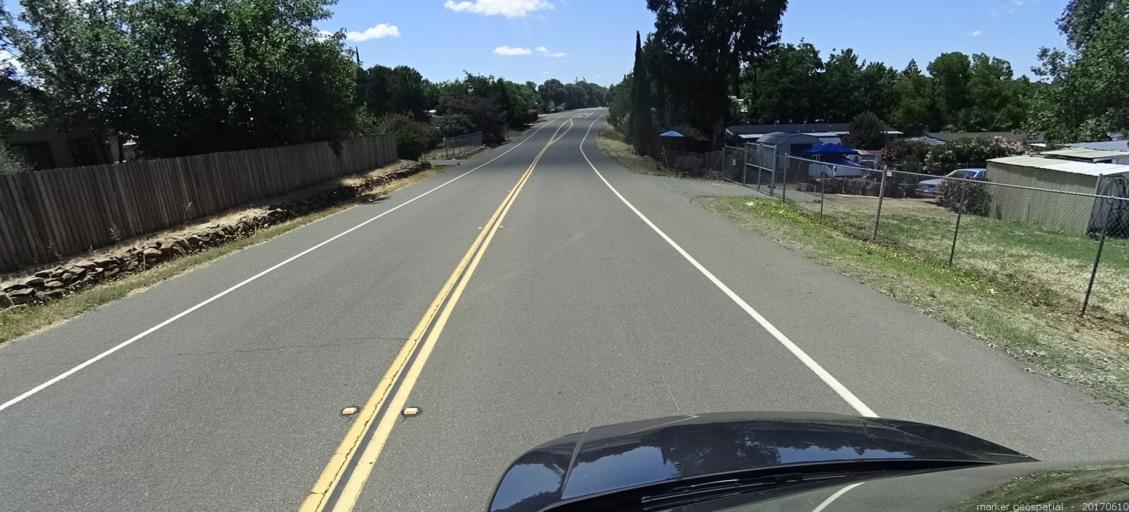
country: US
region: California
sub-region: Butte County
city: Oroville East
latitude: 39.5272
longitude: -121.4671
